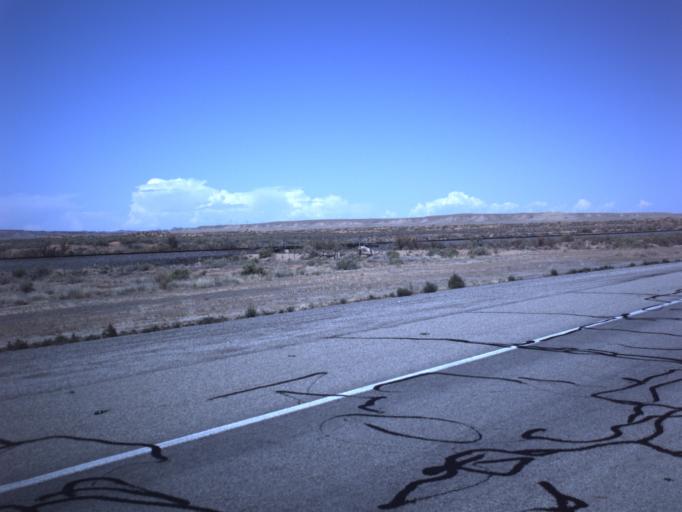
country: US
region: Utah
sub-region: Grand County
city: Moab
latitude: 38.7412
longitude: -109.7348
